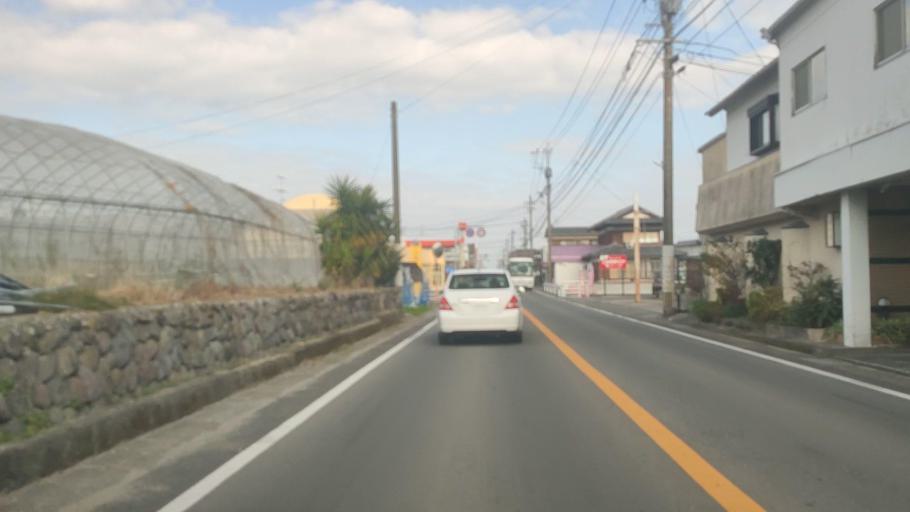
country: JP
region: Nagasaki
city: Shimabara
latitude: 32.7147
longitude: 130.3482
